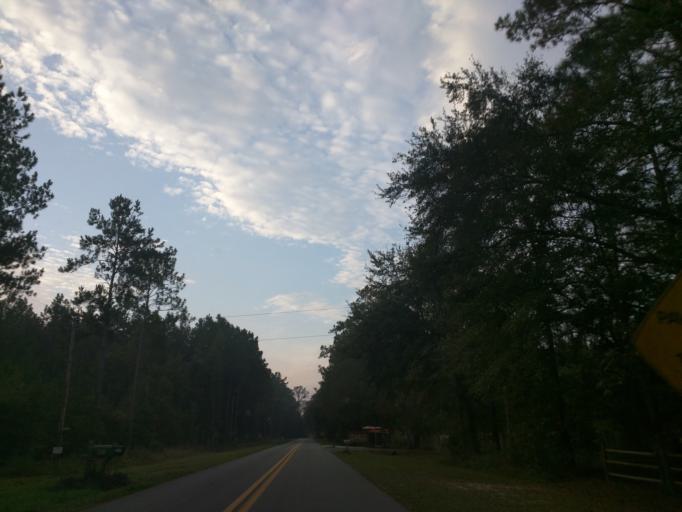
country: US
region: Florida
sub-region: Jefferson County
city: Monticello
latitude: 30.3447
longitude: -83.9908
